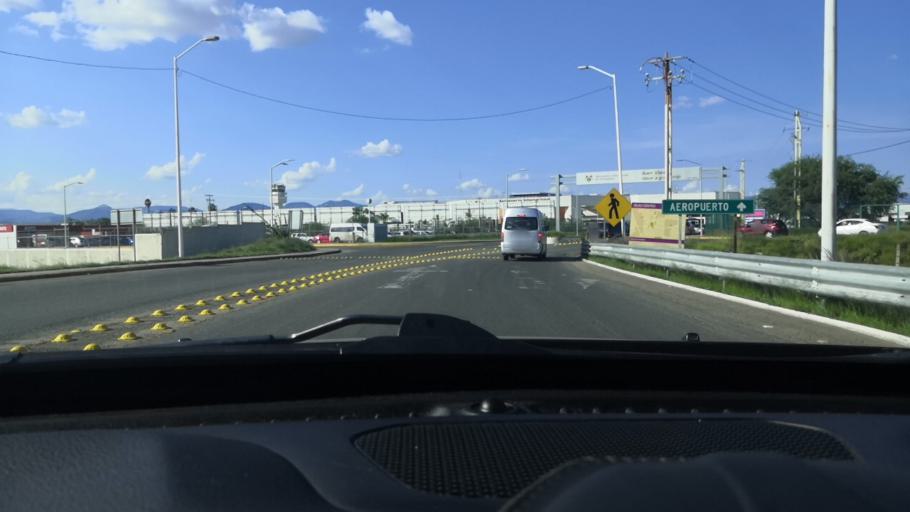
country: MX
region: Guanajuato
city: Colonia Nuevo Mexico
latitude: 20.9832
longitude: -101.4801
